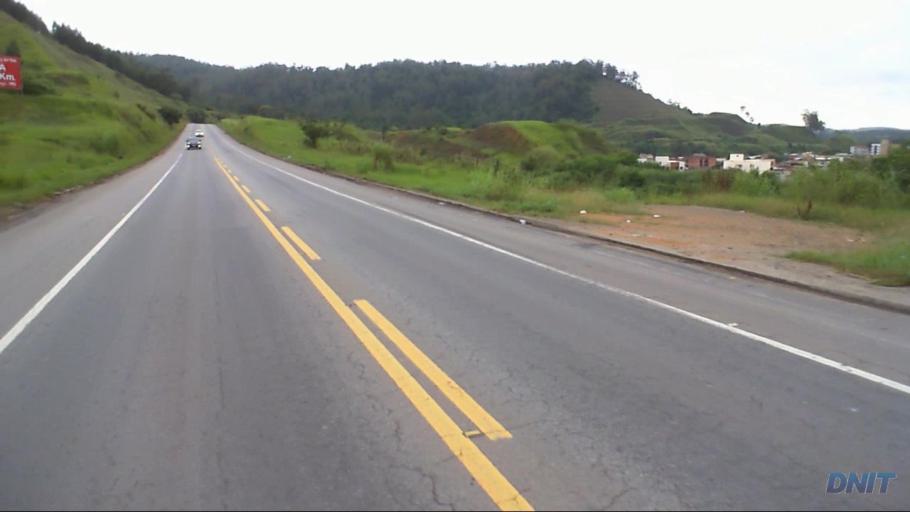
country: BR
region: Minas Gerais
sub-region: Coronel Fabriciano
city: Coronel Fabriciano
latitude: -19.5265
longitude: -42.5802
